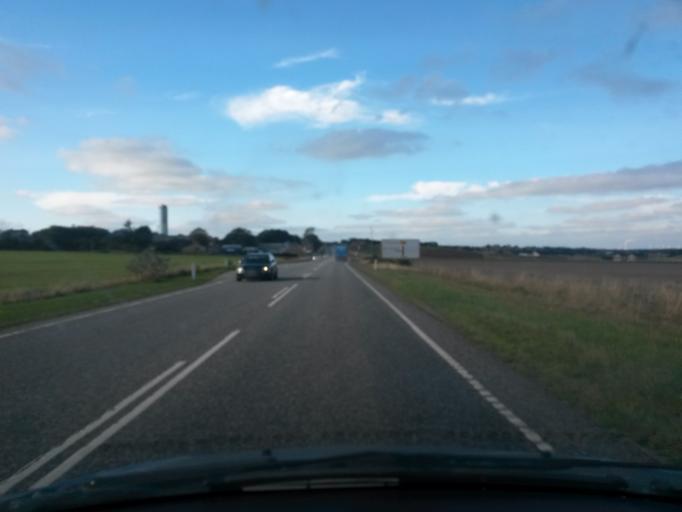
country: DK
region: Central Jutland
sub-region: Holstebro Kommune
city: Holstebro
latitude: 56.3277
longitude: 8.6626
